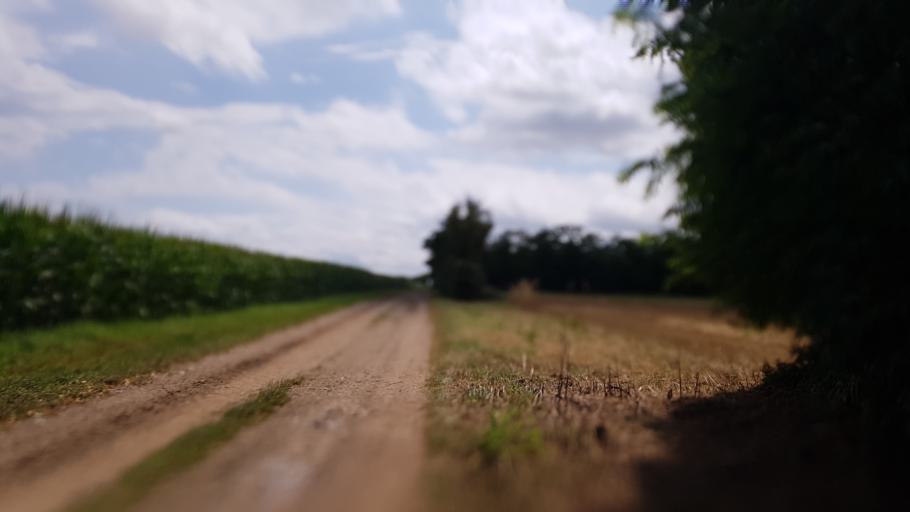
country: FR
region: Rhone-Alpes
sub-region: Departement du Rhone
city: Pusignan
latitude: 45.7240
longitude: 5.0648
